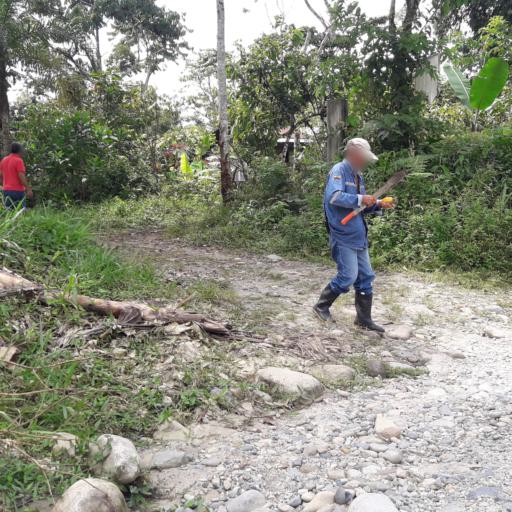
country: EC
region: Napo
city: Archidona
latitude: -0.9423
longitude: -77.8740
